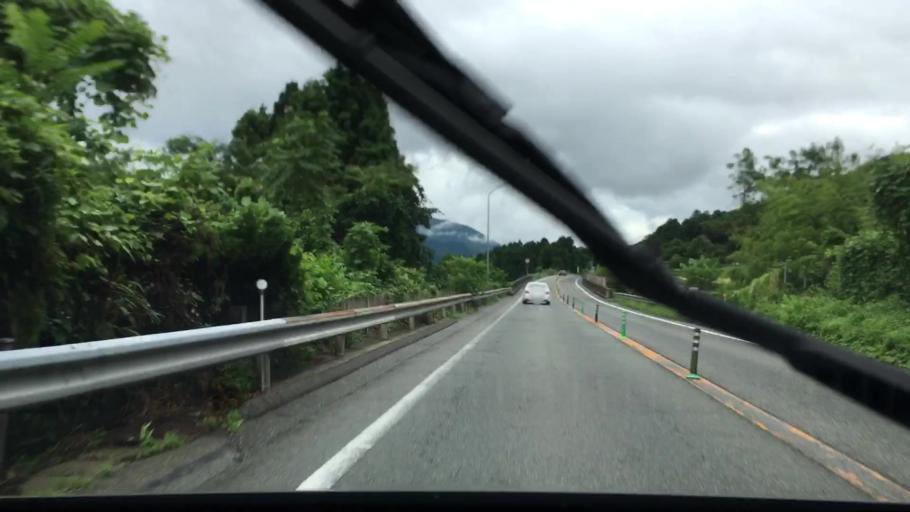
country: JP
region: Hyogo
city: Nishiwaki
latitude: 35.1005
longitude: 134.7772
